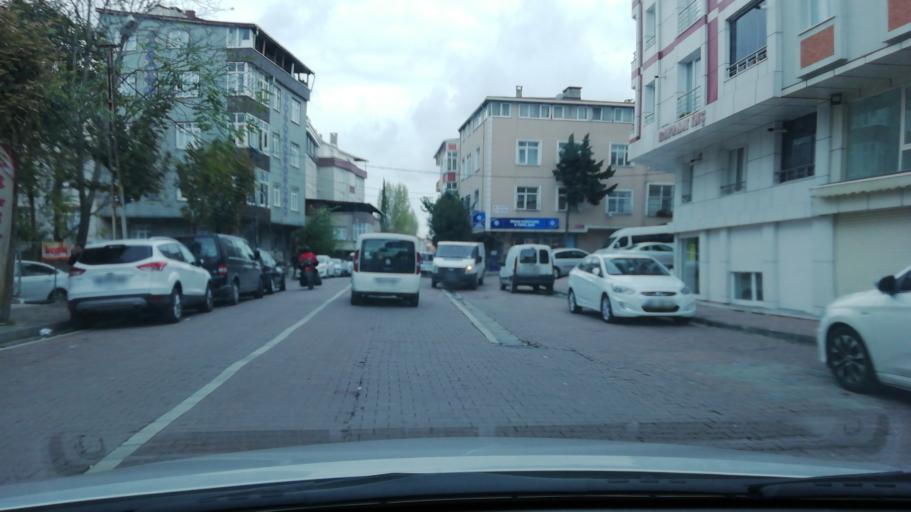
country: TR
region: Istanbul
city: Bahcelievler
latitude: 41.0134
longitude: 28.8311
